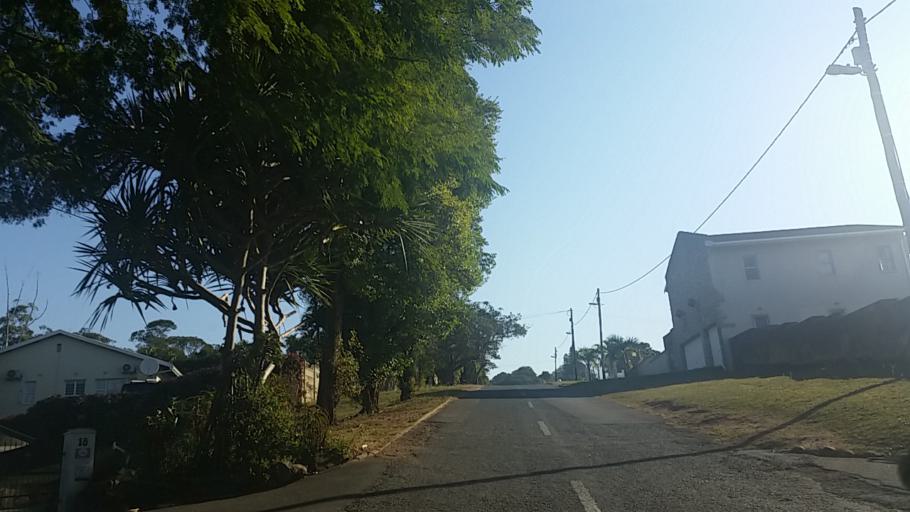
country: ZA
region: KwaZulu-Natal
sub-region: eThekwini Metropolitan Municipality
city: Berea
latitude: -29.8453
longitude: 30.9168
